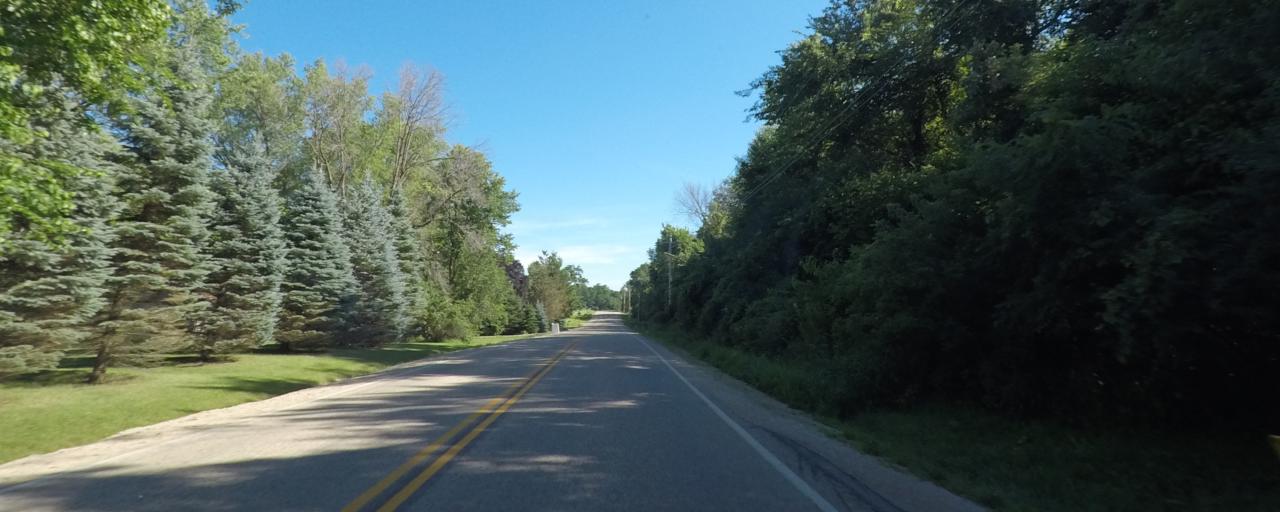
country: US
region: Wisconsin
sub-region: Rock County
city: Edgerton
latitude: 42.7505
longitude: -89.1310
